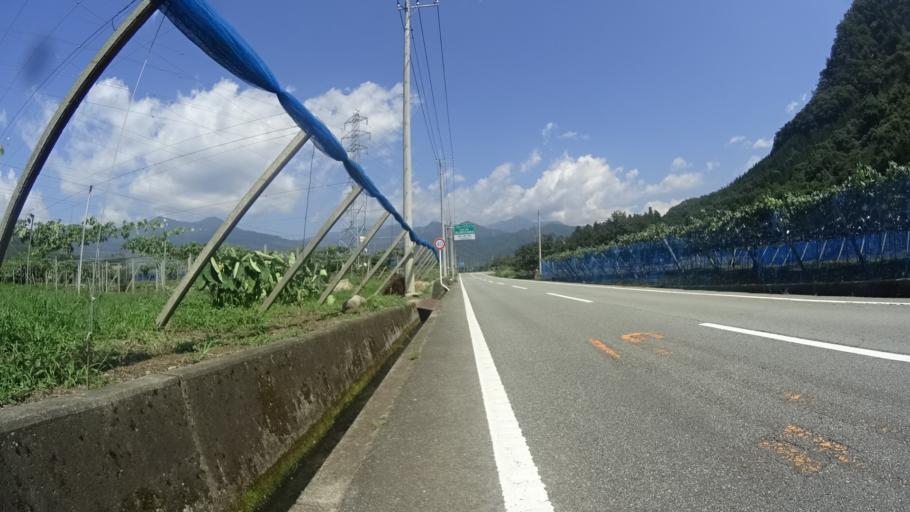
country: JP
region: Yamanashi
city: Enzan
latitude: 35.7344
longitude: 138.7220
